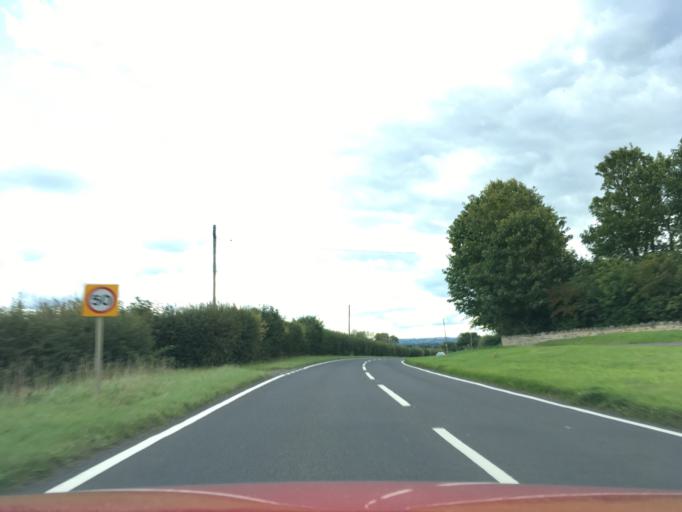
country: GB
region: England
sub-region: South Gloucestershire
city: Alveston
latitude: 51.5770
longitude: -2.5331
